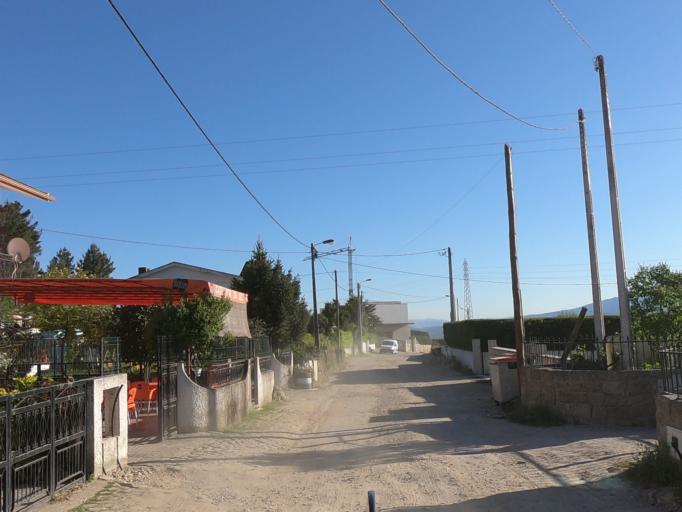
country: PT
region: Vila Real
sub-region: Vila Real
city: Vila Real
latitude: 41.3273
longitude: -7.6929
